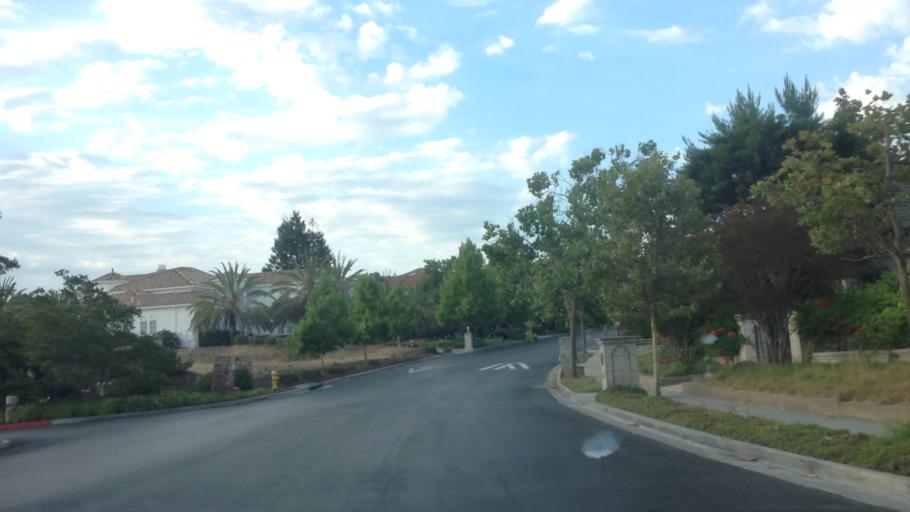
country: US
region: California
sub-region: Santa Clara County
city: Seven Trees
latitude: 37.2750
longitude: -121.7725
